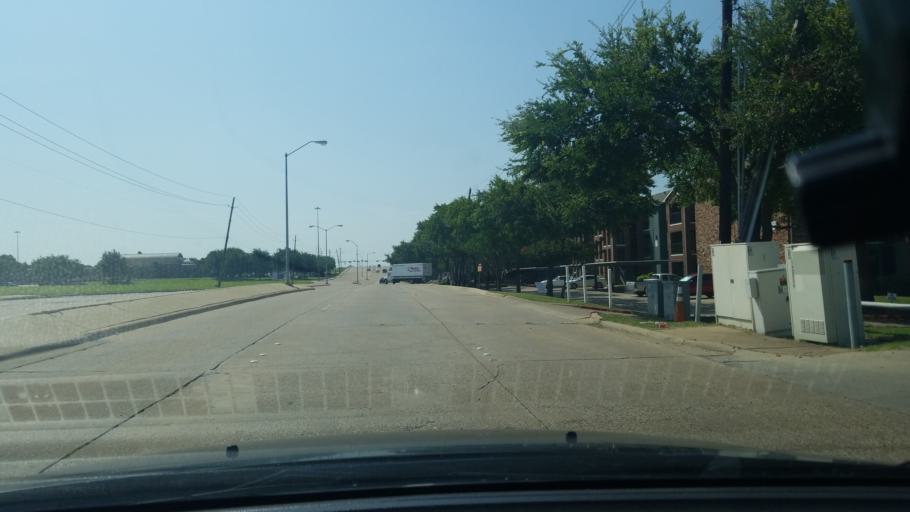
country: US
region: Texas
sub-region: Dallas County
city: Mesquite
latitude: 32.8294
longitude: -96.6290
